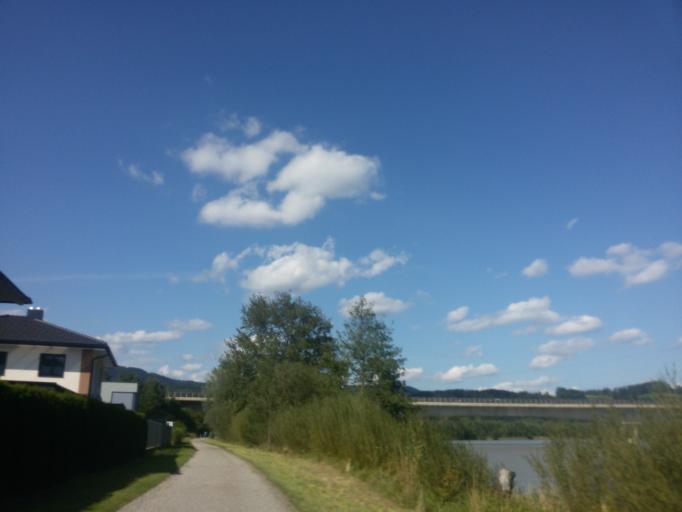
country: AT
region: Carinthia
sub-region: Politischer Bezirk Villach Land
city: Wernberg
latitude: 46.6103
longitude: 13.9184
